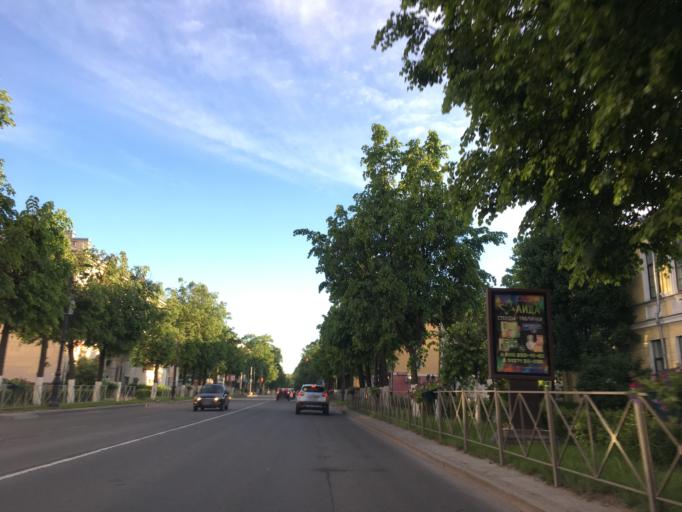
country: RU
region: Leningrad
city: Gatchina
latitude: 59.5736
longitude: 30.1266
